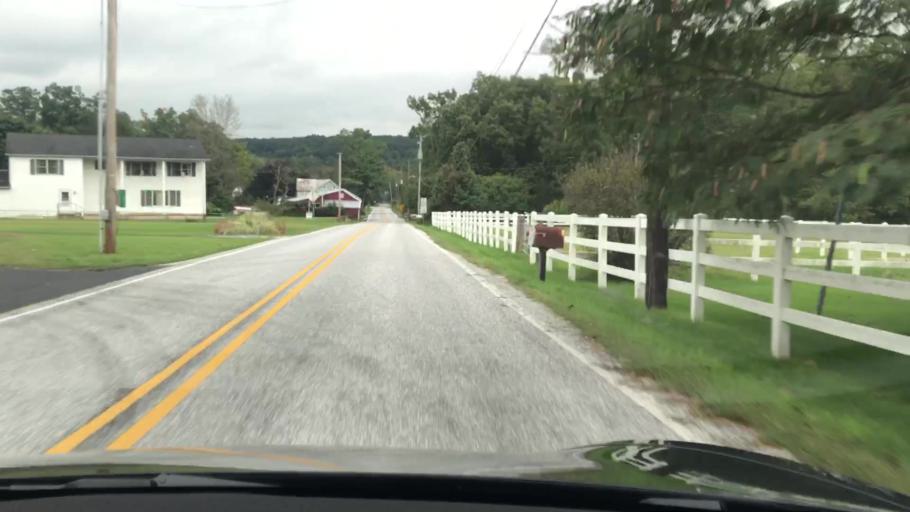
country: US
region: Pennsylvania
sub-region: York County
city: Dillsburg
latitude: 40.0723
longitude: -77.0947
